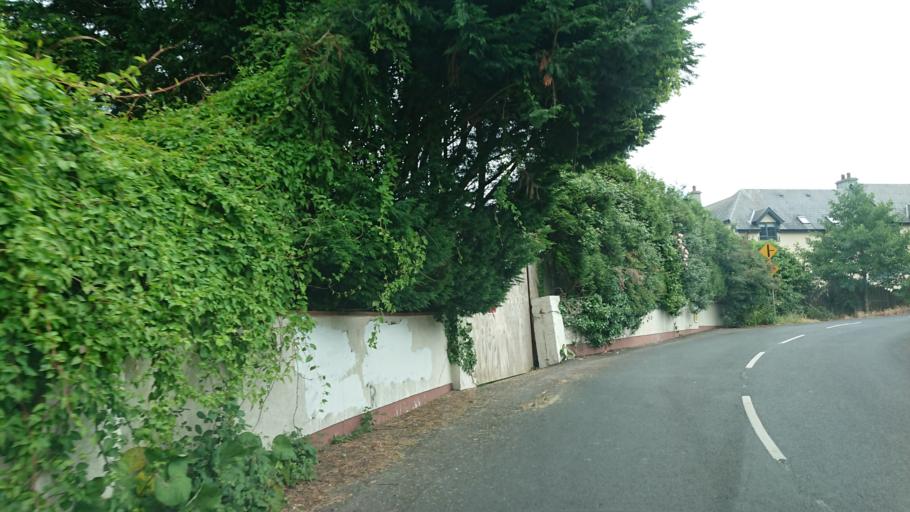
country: IE
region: Munster
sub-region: Waterford
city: Waterford
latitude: 52.2700
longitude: -7.1375
